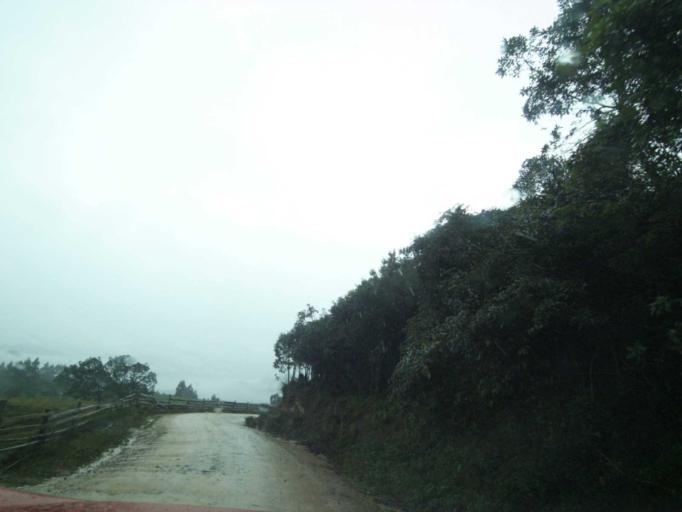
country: BR
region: Santa Catarina
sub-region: Anitapolis
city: Anitapolis
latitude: -27.9278
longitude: -49.1784
